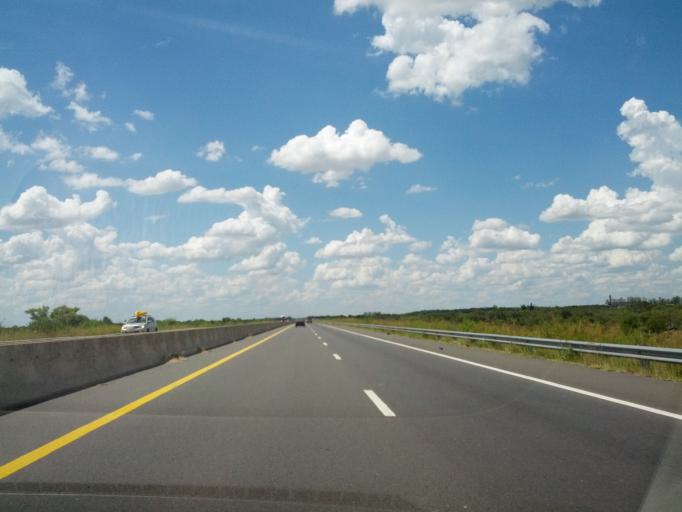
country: AR
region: Entre Rios
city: Colonia Elia
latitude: -32.7587
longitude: -58.4905
